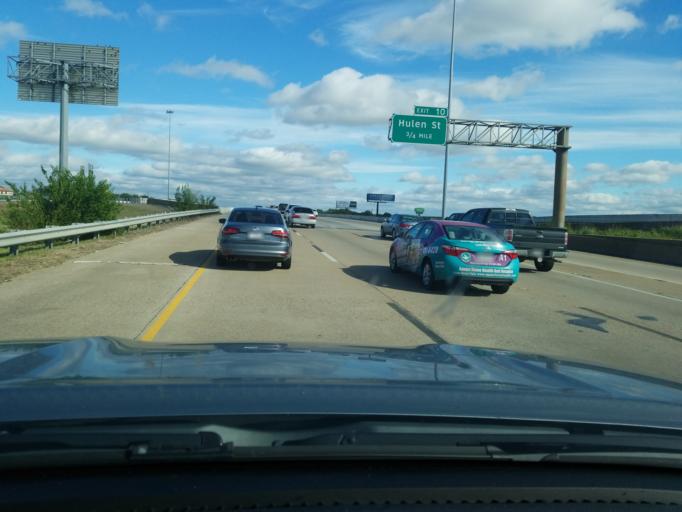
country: US
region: Texas
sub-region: Tarrant County
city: Westworth
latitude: 32.7338
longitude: -97.4056
